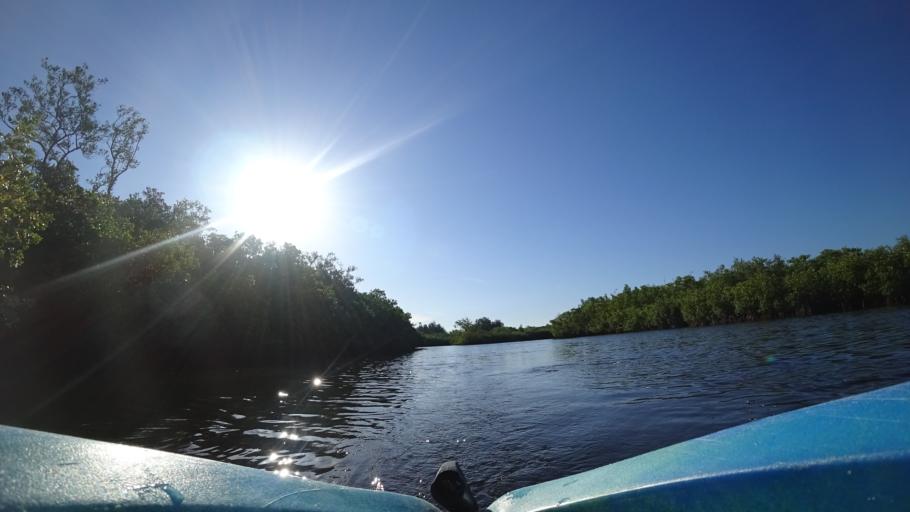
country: US
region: Florida
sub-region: Manatee County
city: West Bradenton
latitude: 27.5195
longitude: -82.6631
